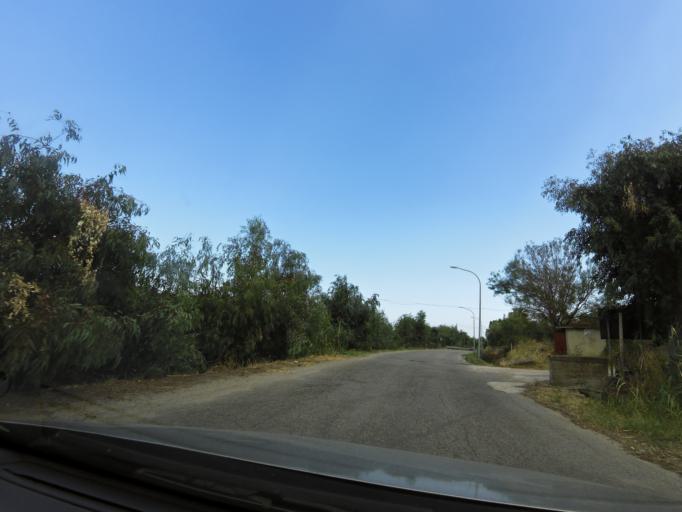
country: IT
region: Calabria
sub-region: Provincia di Reggio Calabria
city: Monasterace Marina
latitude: 38.4211
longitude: 16.5584
